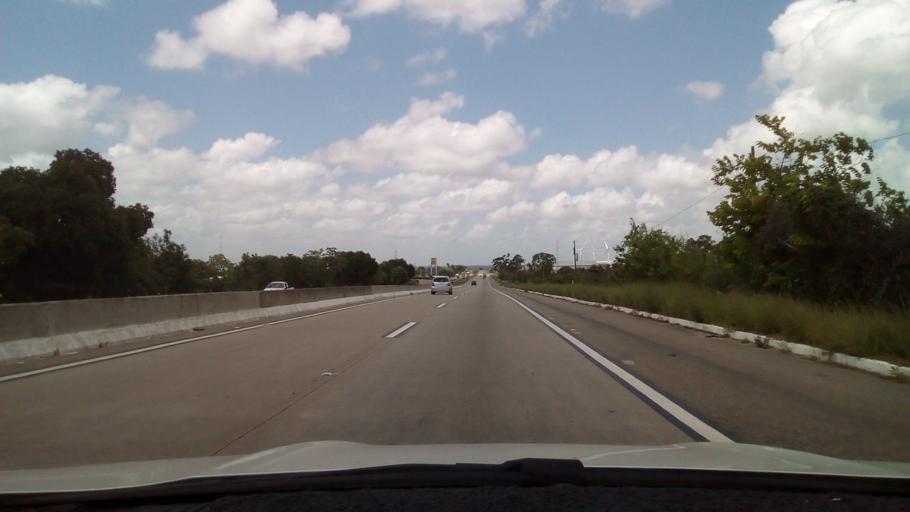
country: BR
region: Paraiba
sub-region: Conde
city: Conde
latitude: -7.2936
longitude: -34.9376
